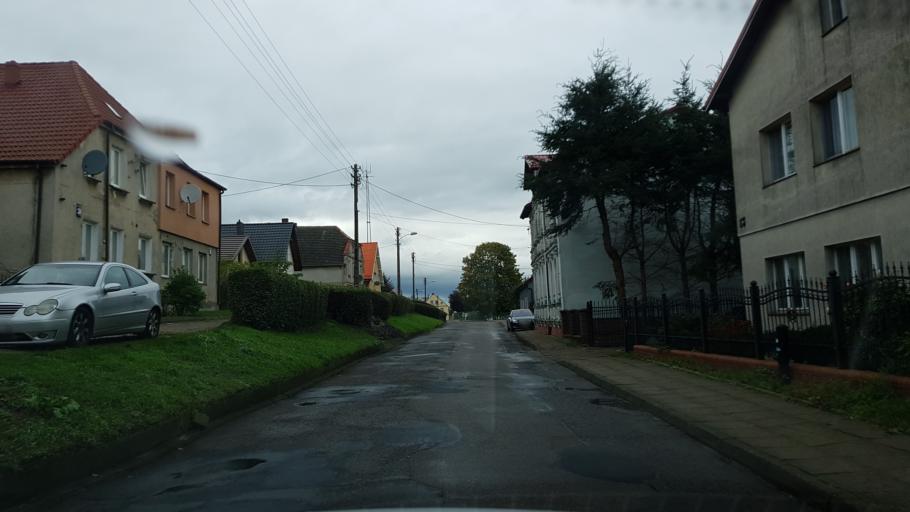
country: PL
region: West Pomeranian Voivodeship
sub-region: Powiat kamienski
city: Wolin
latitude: 53.8371
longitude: 14.6147
